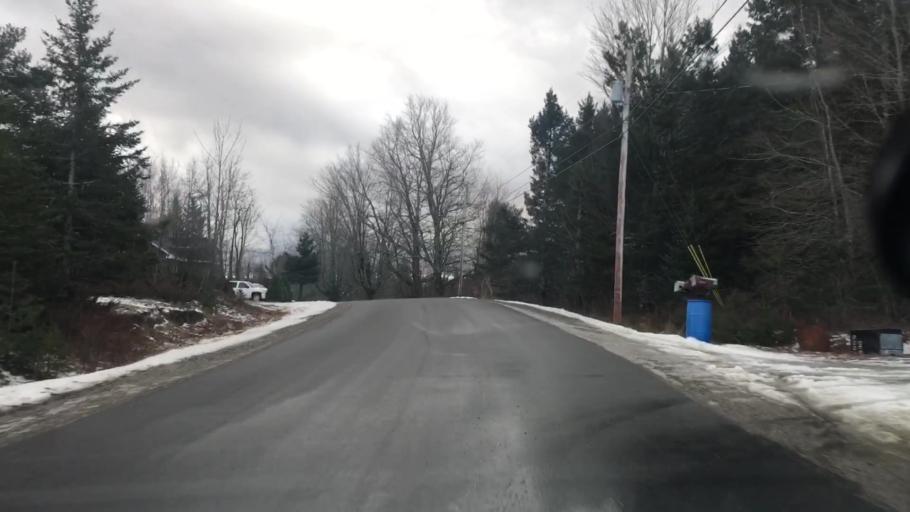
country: US
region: Maine
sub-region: Hancock County
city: Dedham
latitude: 44.6599
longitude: -68.7049
